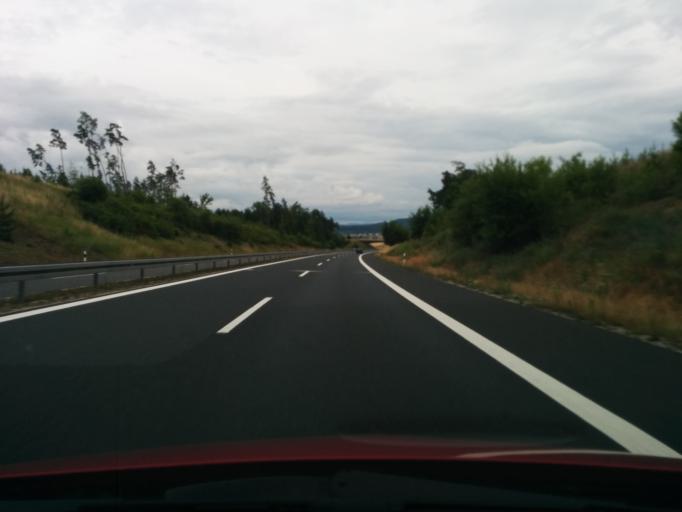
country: DE
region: Bavaria
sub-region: Upper Franconia
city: Lautertal
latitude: 50.3179
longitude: 10.9569
